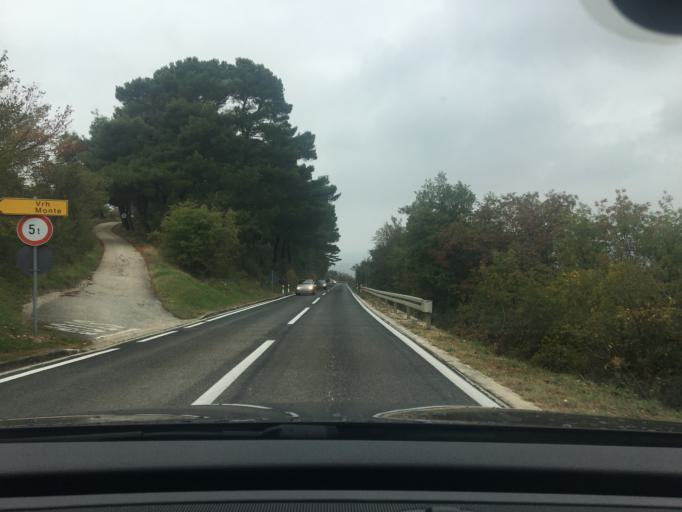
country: HR
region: Istarska
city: Buje
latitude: 45.4475
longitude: 13.6580
